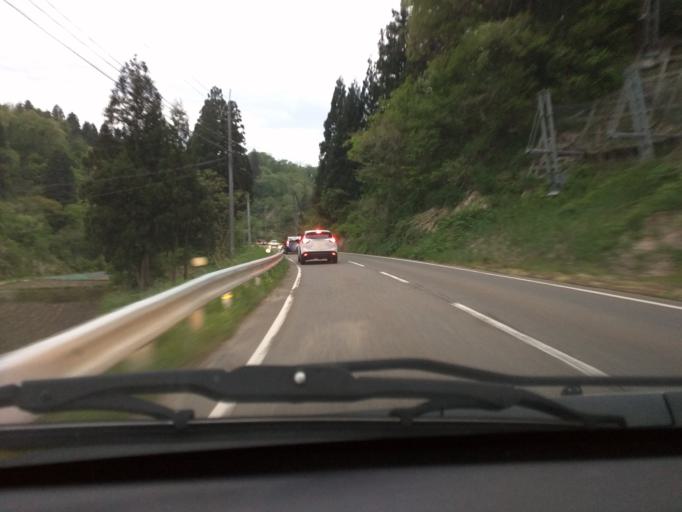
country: JP
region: Niigata
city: Ojiya
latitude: 37.3152
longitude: 138.7406
